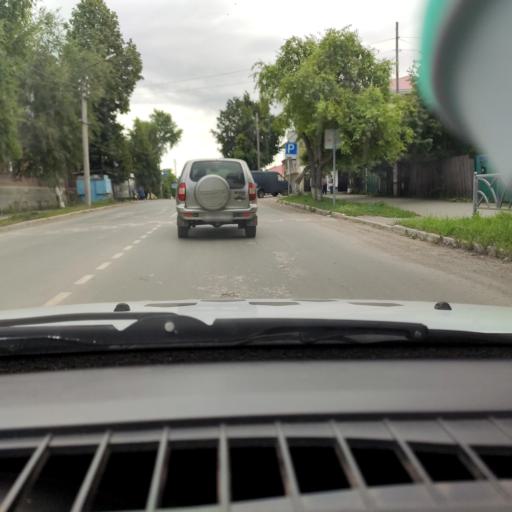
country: RU
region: Sverdlovsk
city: Krasnoufimsk
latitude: 56.6218
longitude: 57.7688
